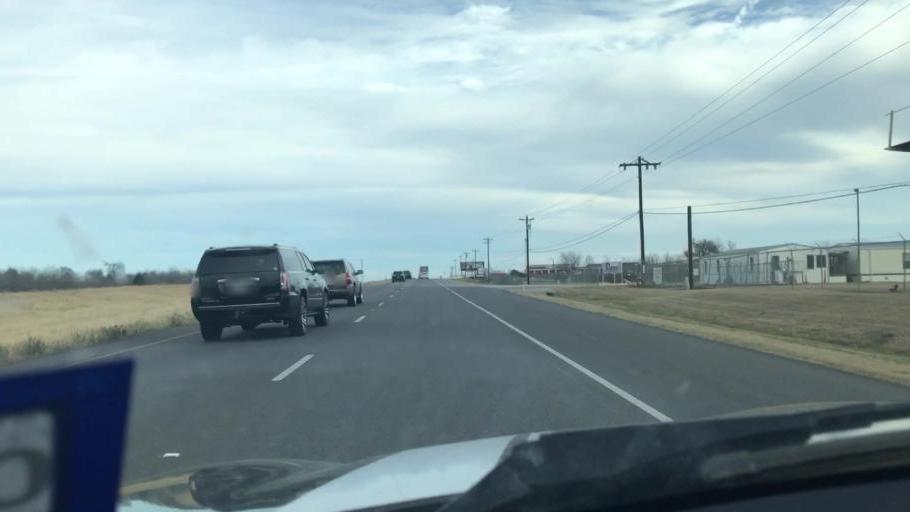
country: US
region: Texas
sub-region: Travis County
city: Manor
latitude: 30.3506
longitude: -97.4955
